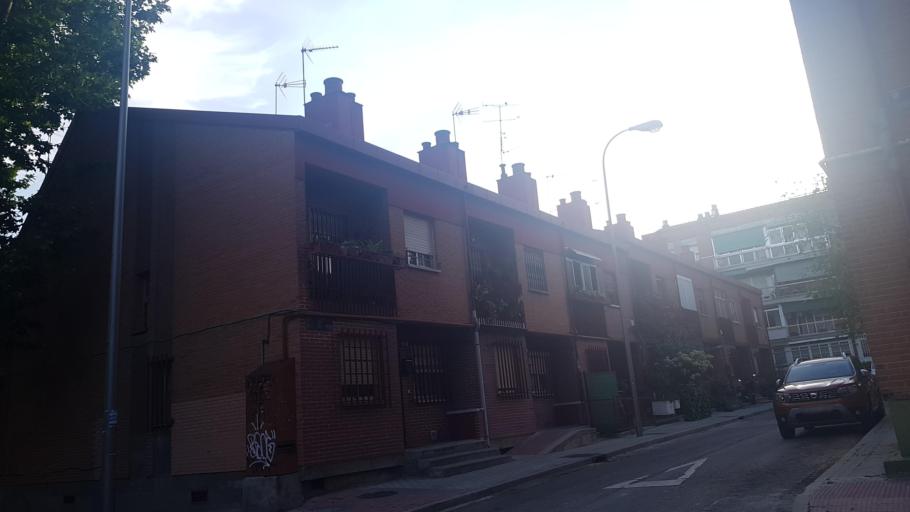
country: ES
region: Madrid
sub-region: Provincia de Madrid
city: Puente de Vallecas
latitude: 40.3722
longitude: -3.6612
